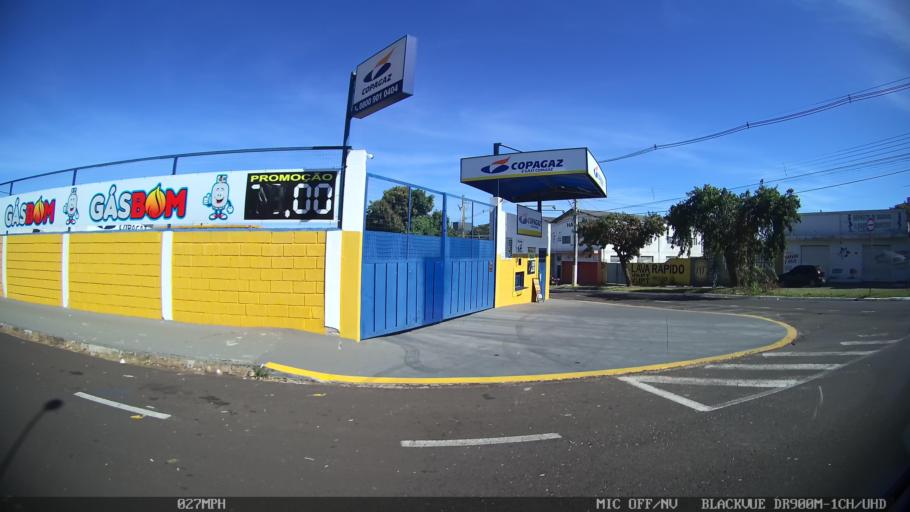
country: BR
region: Sao Paulo
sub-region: Franca
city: Franca
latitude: -20.5444
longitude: -47.3903
